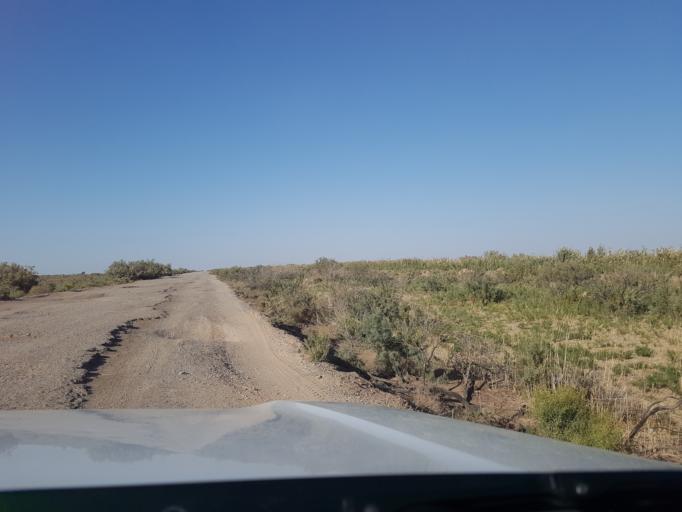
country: IR
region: Razavi Khorasan
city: Sarakhs
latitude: 36.9553
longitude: 61.3810
